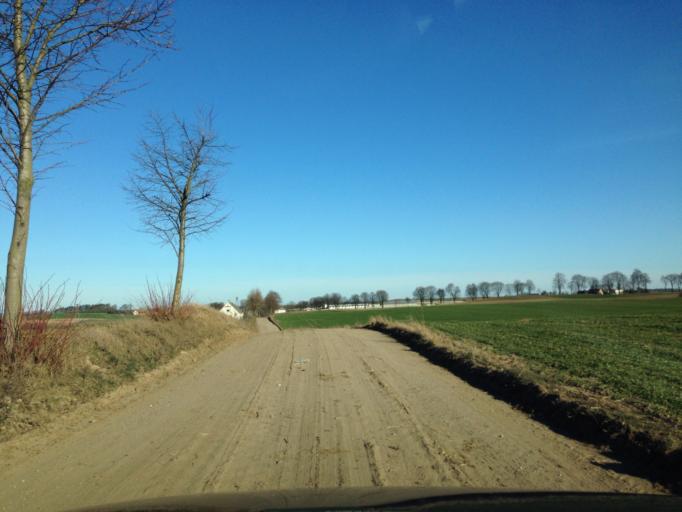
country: PL
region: Kujawsko-Pomorskie
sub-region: Powiat brodnicki
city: Brzozie
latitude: 53.3459
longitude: 19.6467
